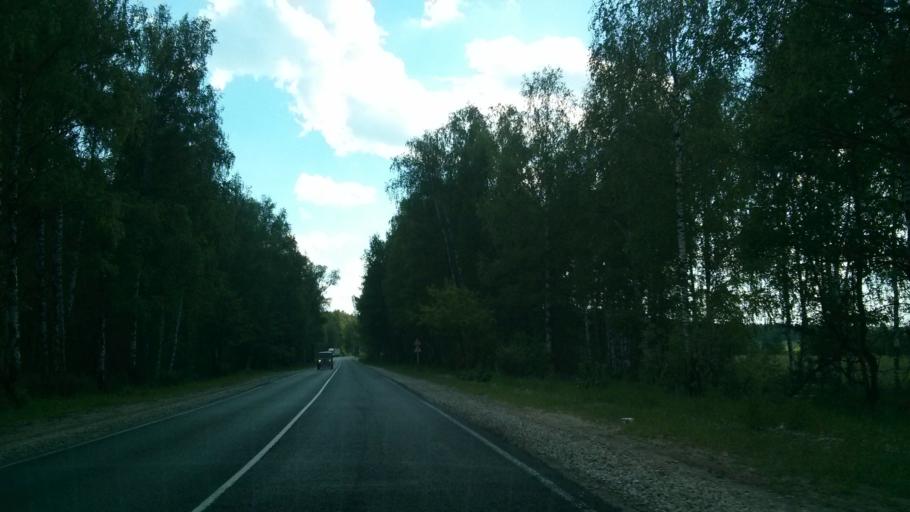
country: RU
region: Vladimir
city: Murom
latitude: 55.5144
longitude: 41.9273
